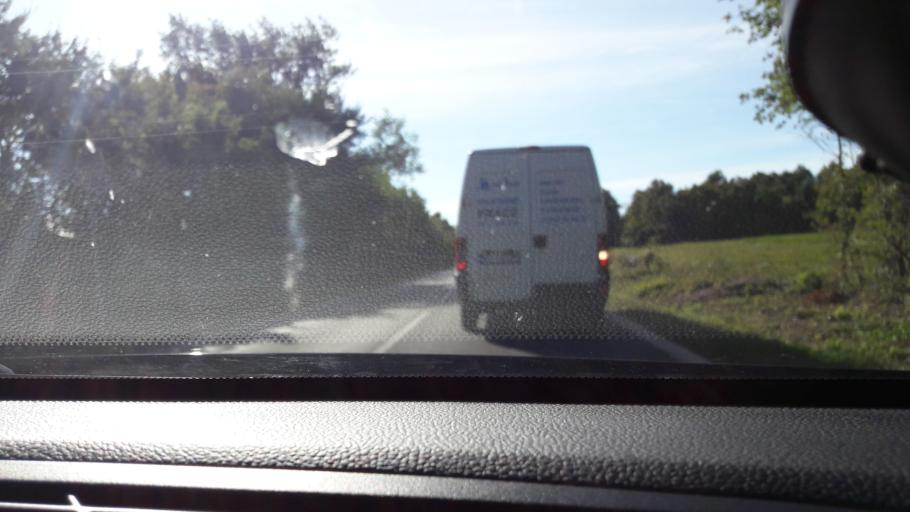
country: SK
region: Kosicky
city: Vinne
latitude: 48.8110
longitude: 22.0434
